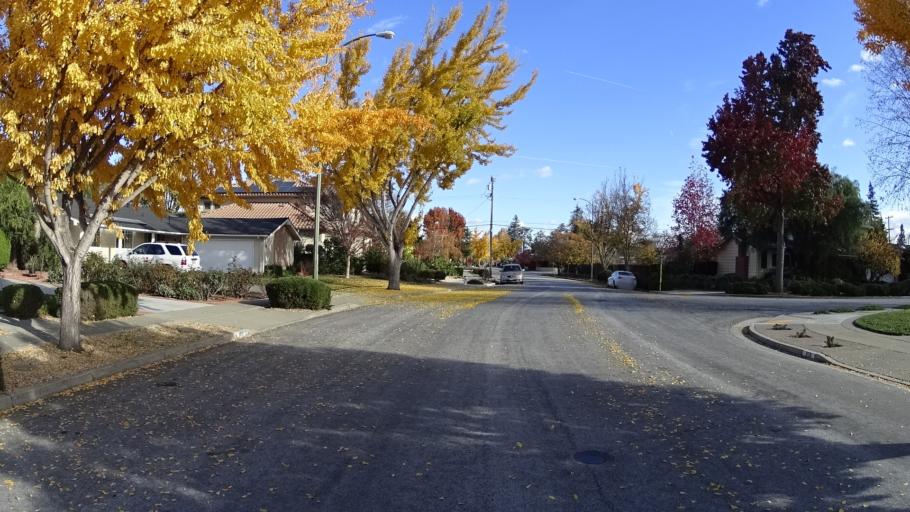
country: US
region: California
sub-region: Santa Clara County
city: Cupertino
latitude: 37.3412
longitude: -122.0524
